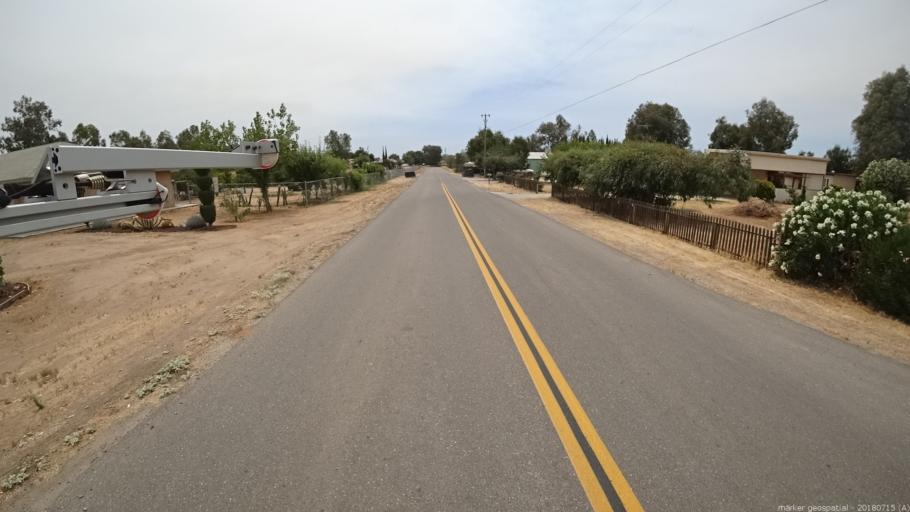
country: US
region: California
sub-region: Madera County
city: Madera Acres
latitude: 37.0036
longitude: -120.0924
